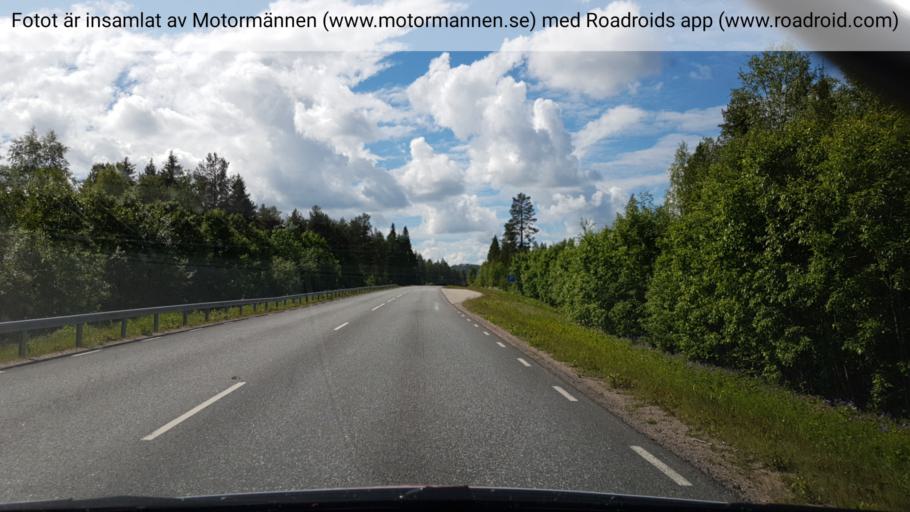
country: FI
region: Lapland
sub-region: Torniolaakso
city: Ylitornio
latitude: 66.3349
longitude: 23.6415
